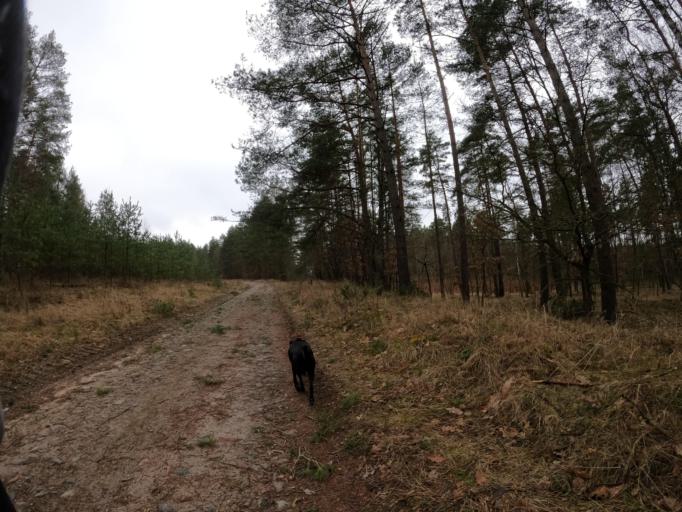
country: PL
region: Greater Poland Voivodeship
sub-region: Powiat zlotowski
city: Sypniewo
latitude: 53.4996
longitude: 16.5602
